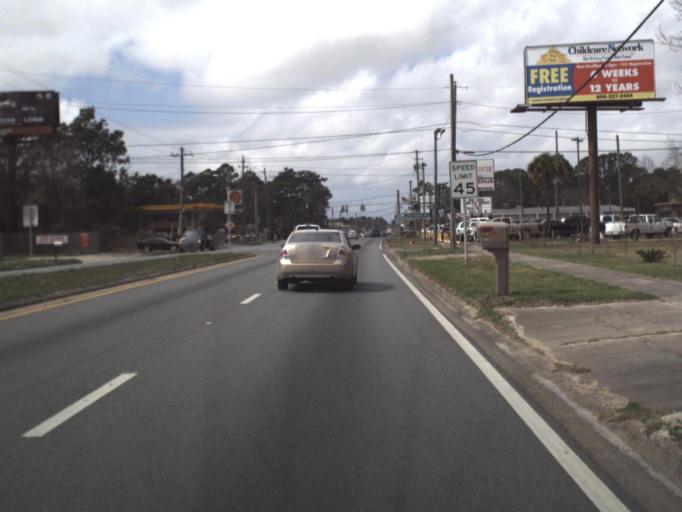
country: US
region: Florida
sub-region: Bay County
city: Cedar Grove
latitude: 30.1750
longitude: -85.6231
